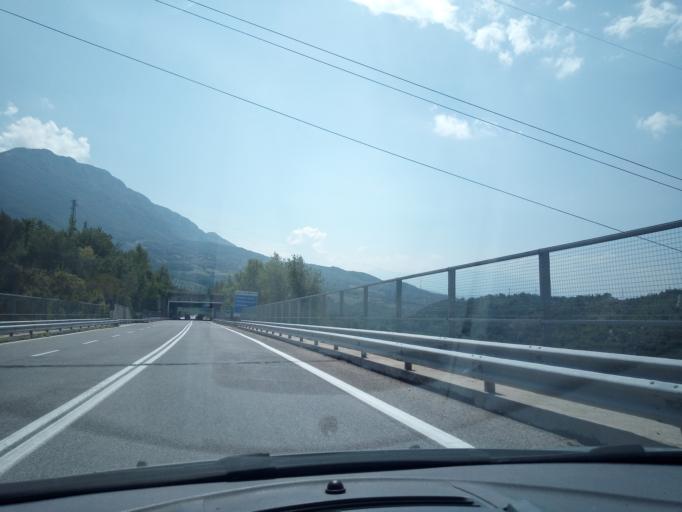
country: IT
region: Campania
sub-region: Provincia di Avellino
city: Calabritto
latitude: 40.7893
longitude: 15.2401
